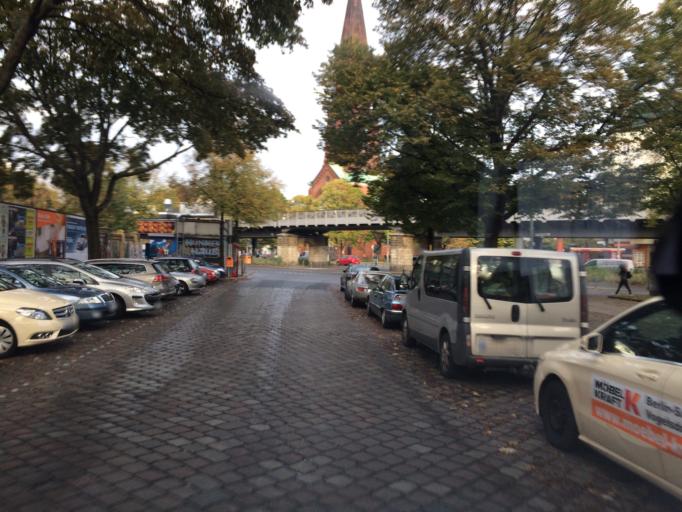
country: DE
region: Berlin
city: Berlin Treptow
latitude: 52.4991
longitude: 13.4329
